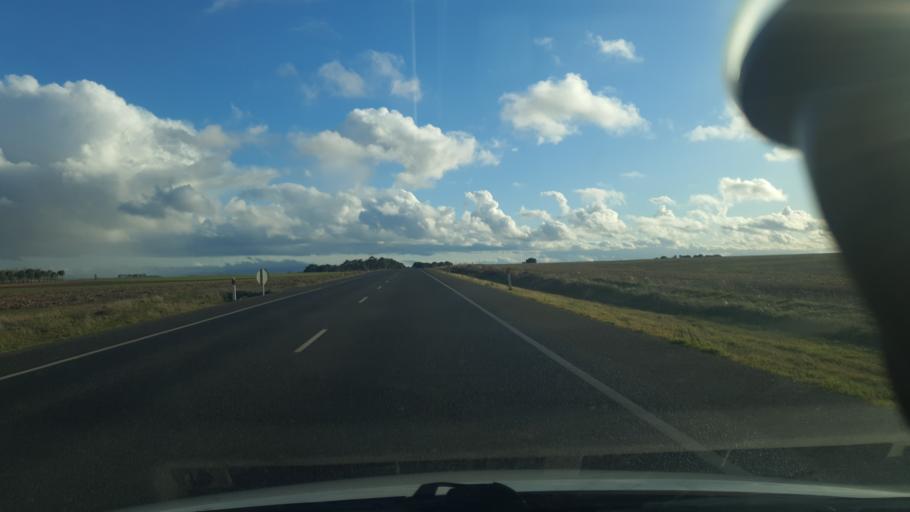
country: ES
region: Castille and Leon
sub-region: Provincia de Segovia
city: Rapariegos
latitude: 41.0766
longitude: -4.6345
